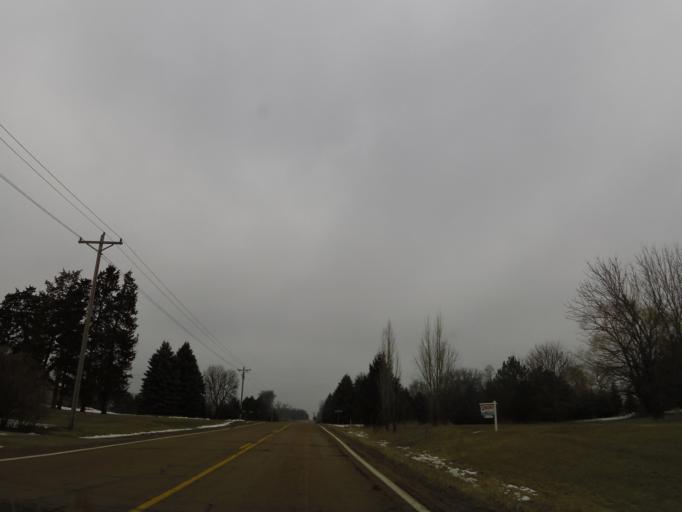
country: US
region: Minnesota
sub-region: Scott County
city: Prior Lake
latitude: 44.6836
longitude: -93.4606
